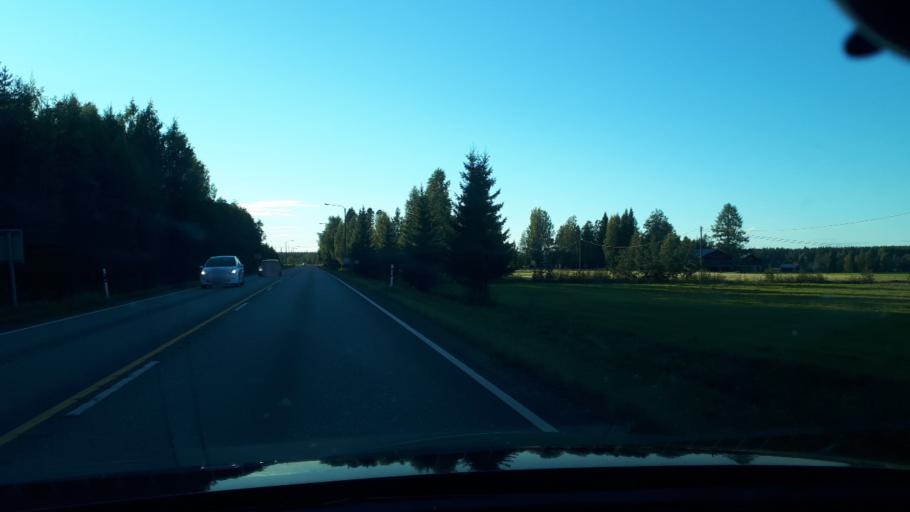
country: FI
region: Northern Savo
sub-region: Ylae-Savo
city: Vieremae
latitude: 63.6672
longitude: 27.0668
